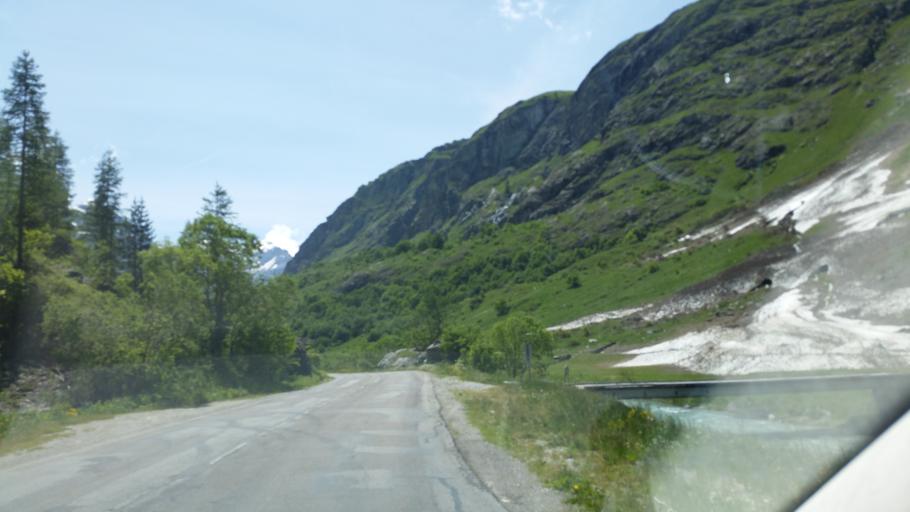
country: FR
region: Rhone-Alpes
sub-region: Departement de la Savoie
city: Val-d'Isere
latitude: 45.3575
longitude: 7.0304
